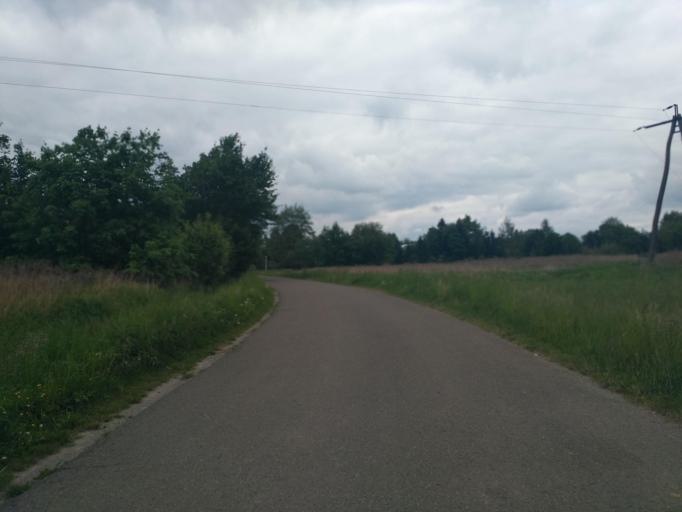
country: PL
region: Subcarpathian Voivodeship
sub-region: Powiat krosnienski
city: Jedlicze
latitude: 49.6964
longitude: 21.6692
